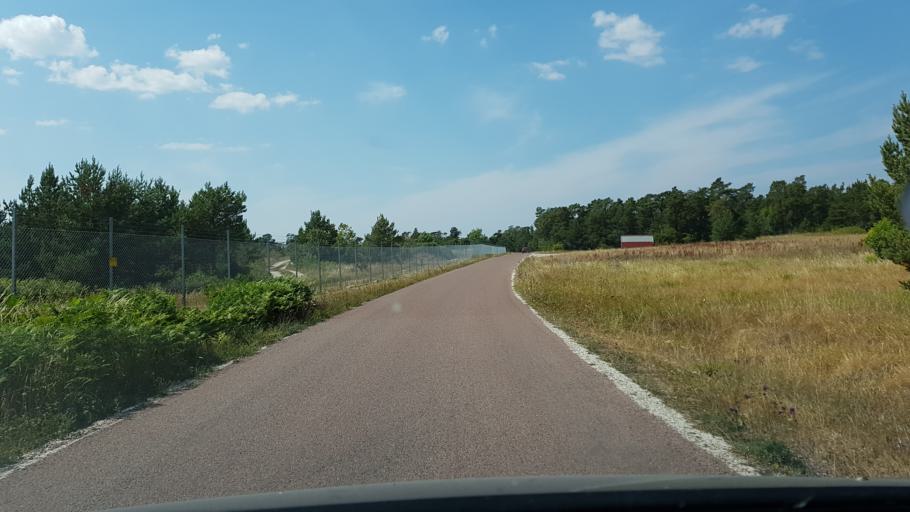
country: SE
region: Gotland
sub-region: Gotland
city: Visby
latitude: 57.6841
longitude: 18.3621
